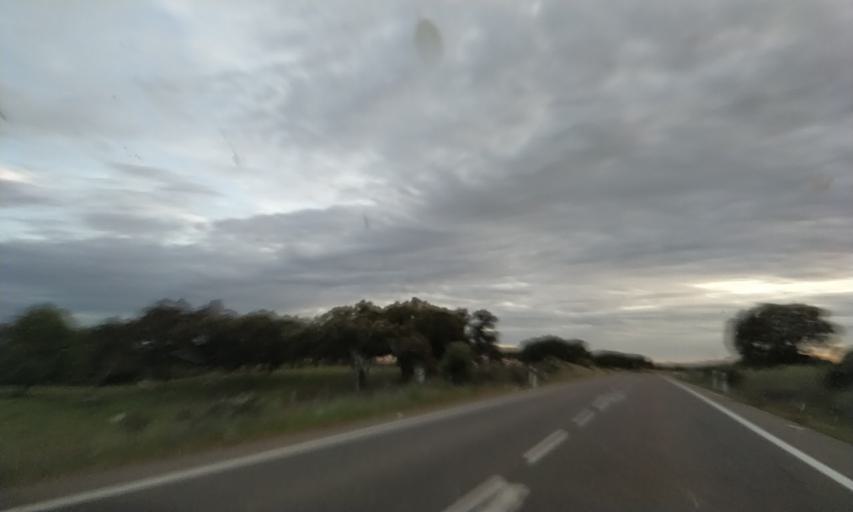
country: ES
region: Extremadura
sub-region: Provincia de Badajoz
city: La Roca de la Sierra
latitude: 39.0673
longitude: -6.7604
